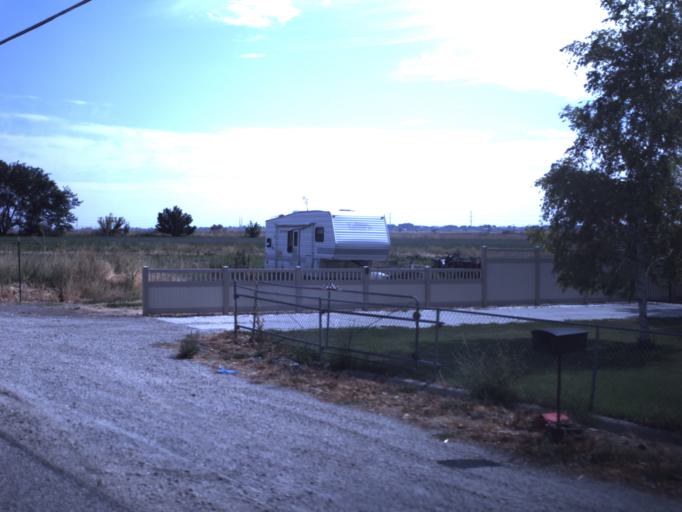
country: US
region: Utah
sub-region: Box Elder County
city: Honeyville
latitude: 41.6300
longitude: -112.0770
